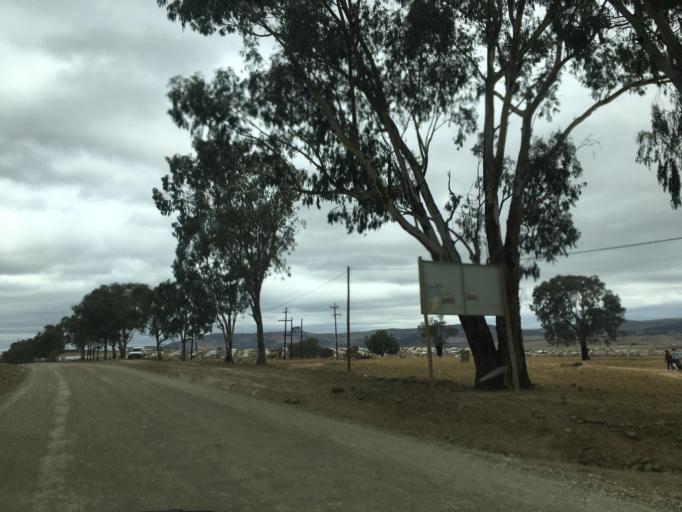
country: ZA
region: Eastern Cape
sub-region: Chris Hani District Municipality
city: Cala
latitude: -31.5343
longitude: 27.6890
